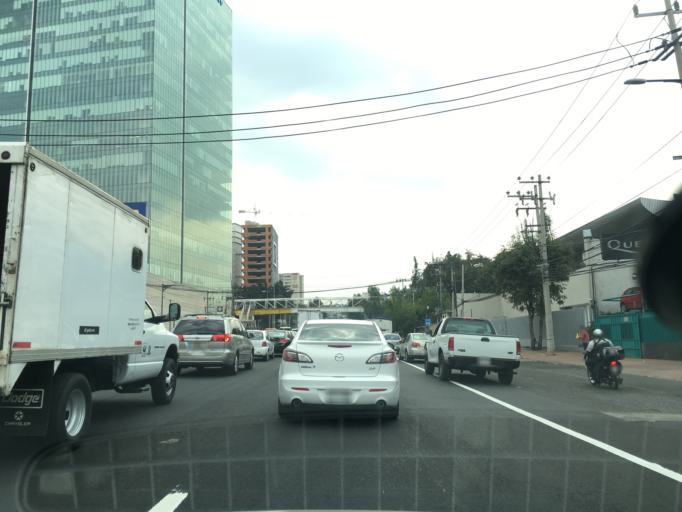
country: MX
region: Mexico City
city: Cuajimalpa
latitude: 19.3640
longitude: -99.2800
